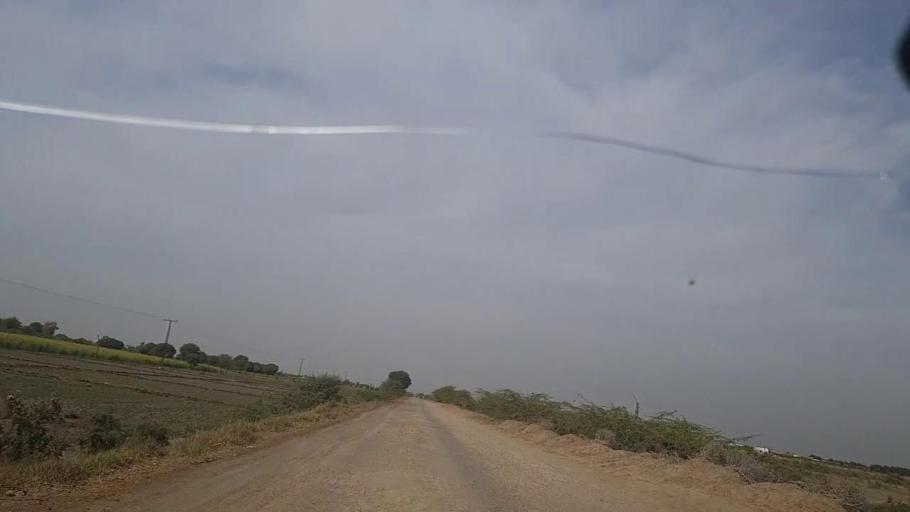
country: PK
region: Sindh
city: Pithoro
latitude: 25.5562
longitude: 69.3628
